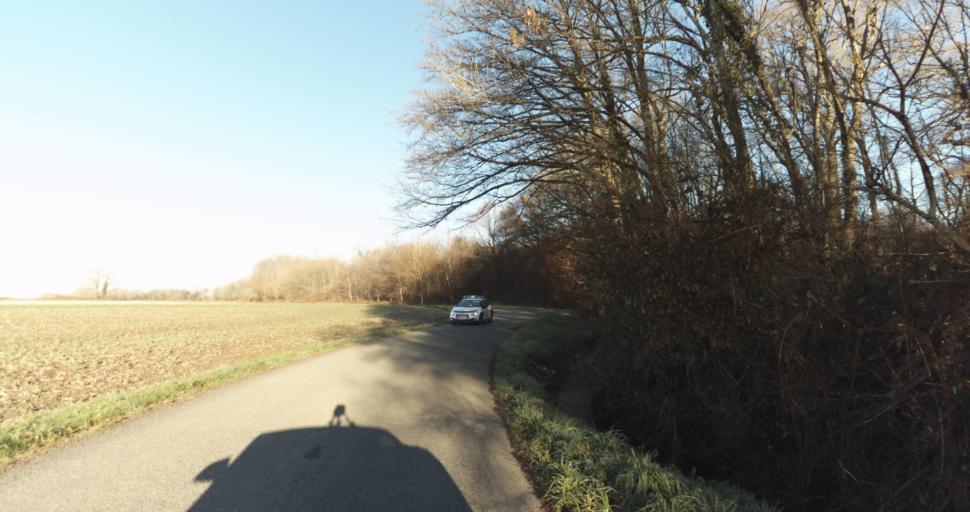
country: FR
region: Aquitaine
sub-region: Departement des Pyrenees-Atlantiques
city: Ousse
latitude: 43.3128
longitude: -0.2540
